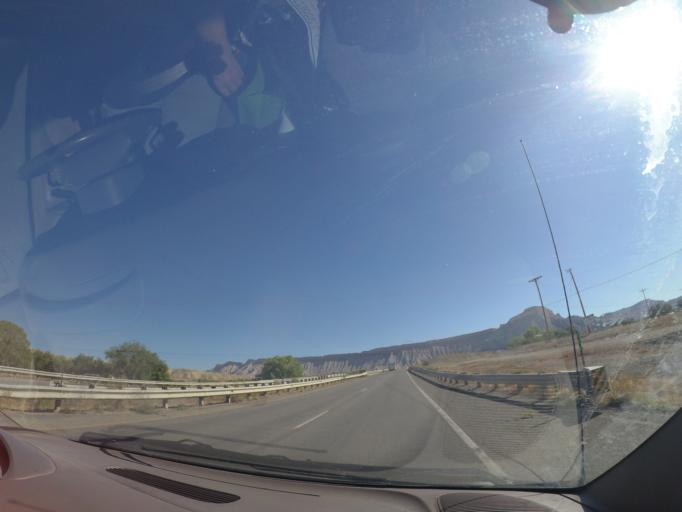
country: US
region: Colorado
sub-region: Mesa County
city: Clifton
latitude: 39.0996
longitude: -108.4474
